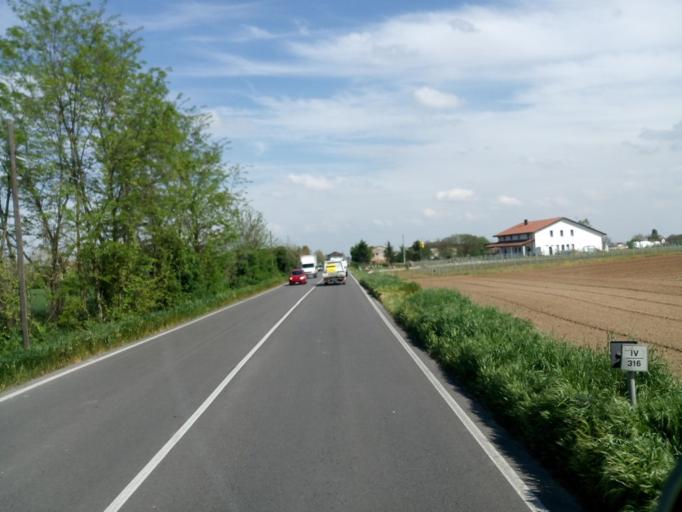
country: IT
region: Veneto
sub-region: Provincia di Verona
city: Sanguinetto
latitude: 45.1818
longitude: 11.1103
